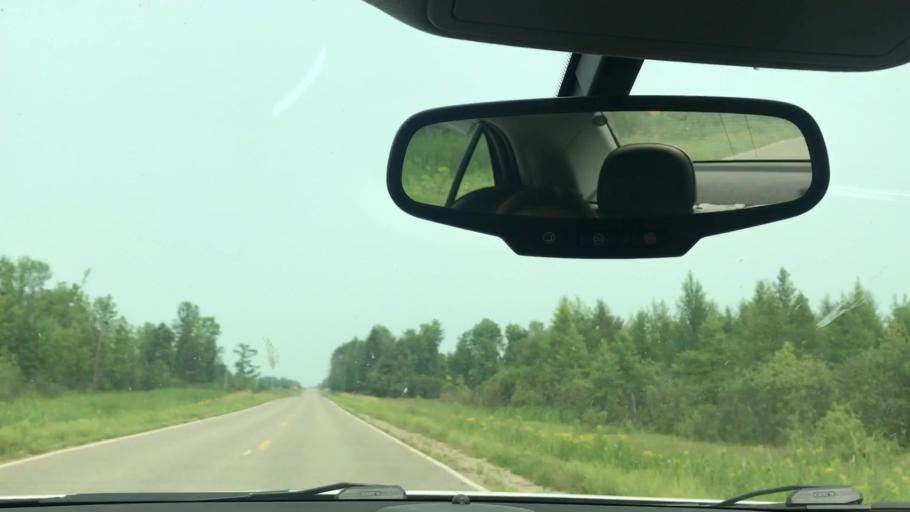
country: US
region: Minnesota
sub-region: Itasca County
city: Cohasset
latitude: 47.3708
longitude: -93.8803
